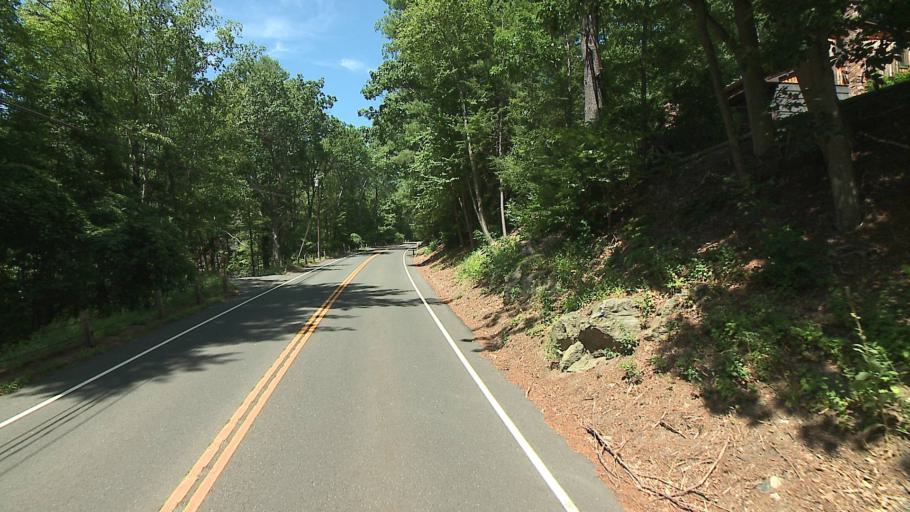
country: US
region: Connecticut
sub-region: Litchfield County
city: New Hartford Center
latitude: 41.9324
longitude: -72.9702
